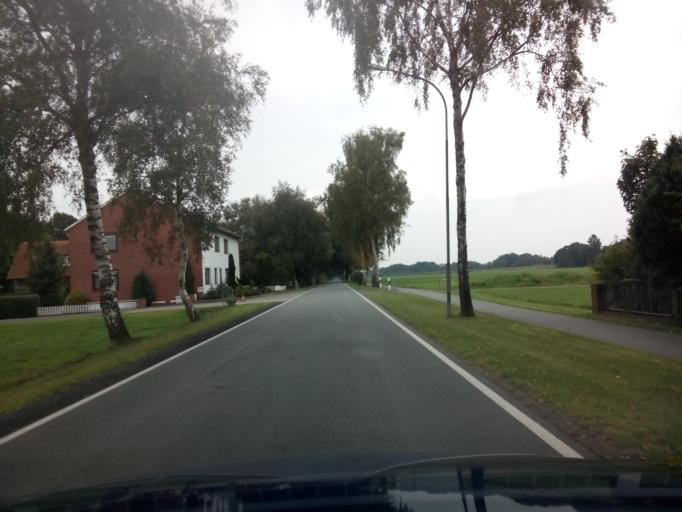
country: DE
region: Lower Saxony
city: Worpswede
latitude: 53.2407
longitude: 8.9810
